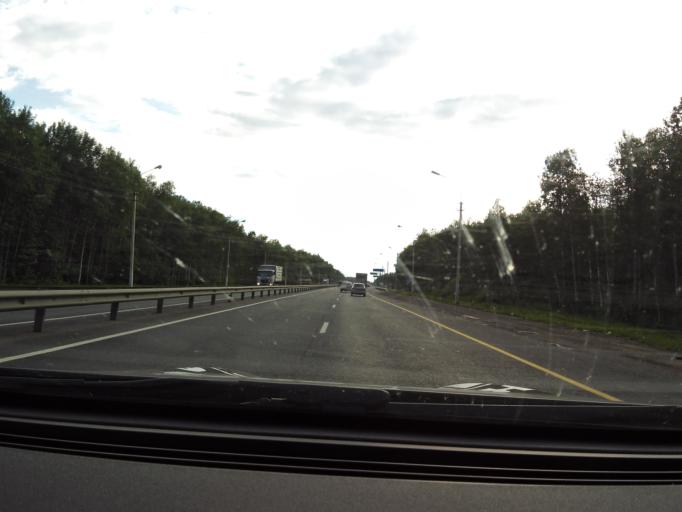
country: RU
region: Vladimir
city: Kameshkovo
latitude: 56.1952
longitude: 40.9713
